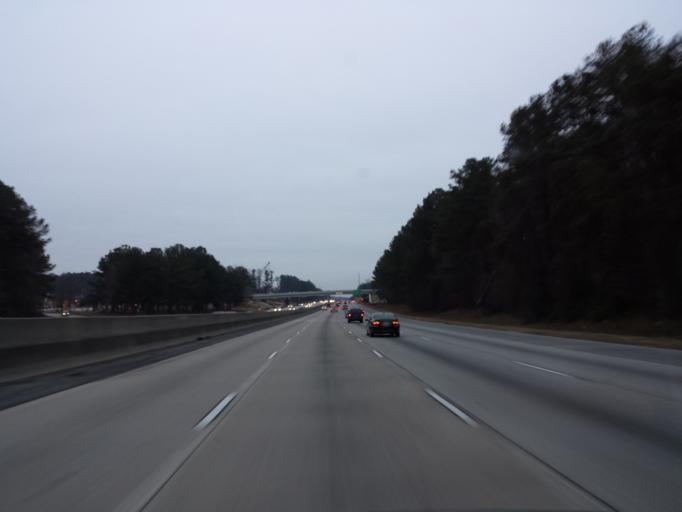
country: US
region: Georgia
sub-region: DeKalb County
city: Dunwoody
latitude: 33.9861
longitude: -84.3399
